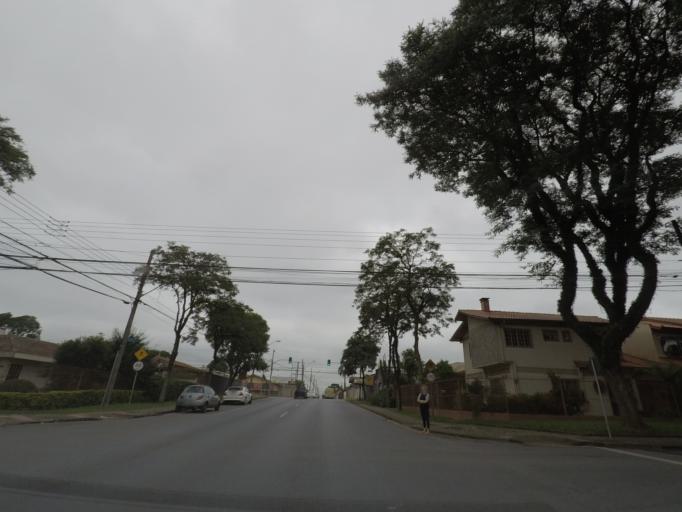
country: BR
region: Parana
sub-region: Curitiba
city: Curitiba
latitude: -25.4781
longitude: -49.3041
